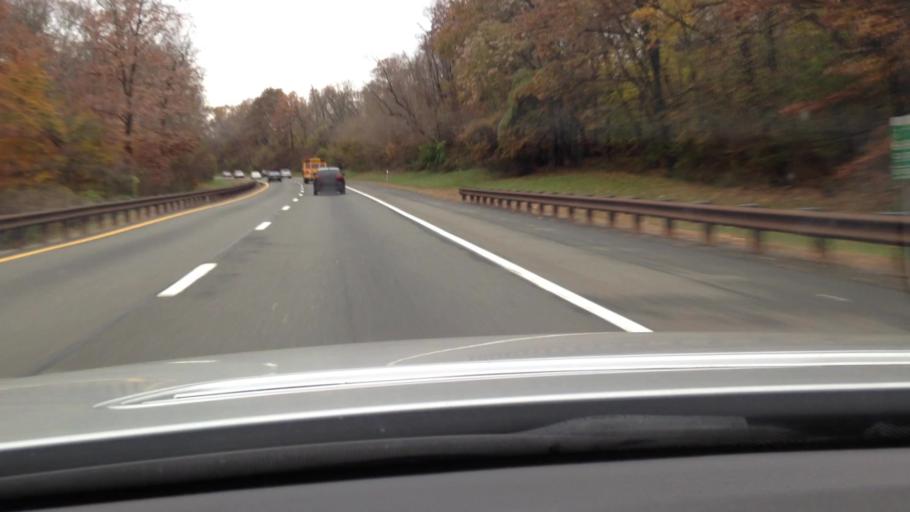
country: US
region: New Jersey
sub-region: Bergen County
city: Woodcliff Lake
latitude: 41.0275
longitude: -74.0692
